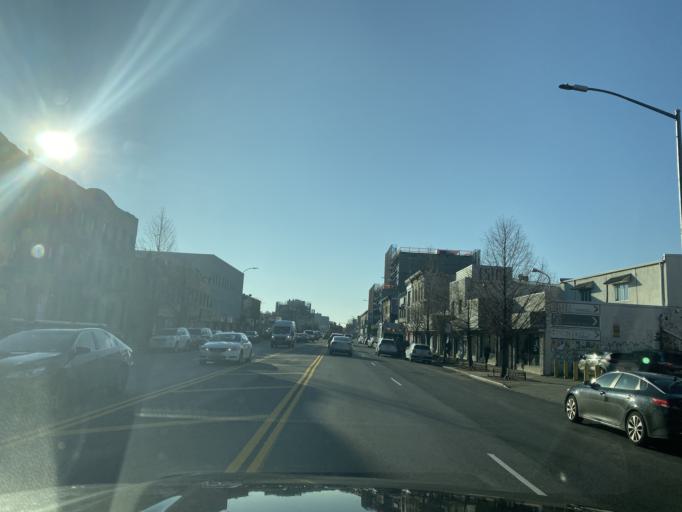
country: US
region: New York
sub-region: Kings County
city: Bensonhurst
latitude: 40.6117
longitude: -73.9628
